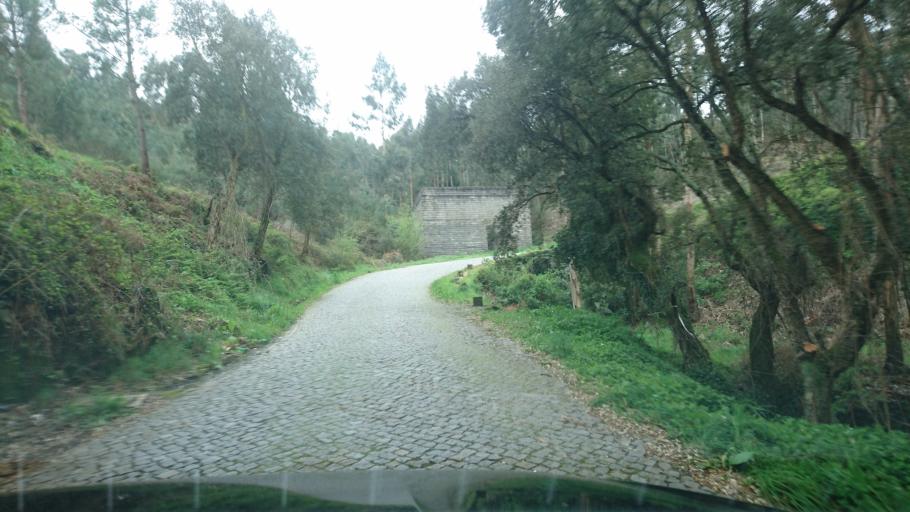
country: PT
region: Porto
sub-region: Paredes
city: Recarei
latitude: 41.1377
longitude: -8.3958
